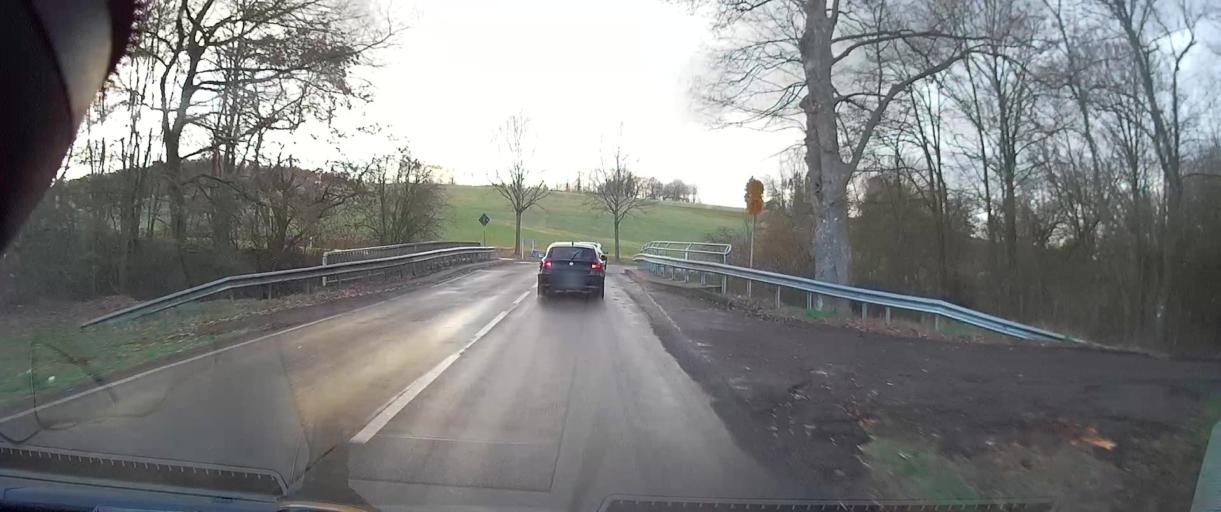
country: DE
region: Rheinland-Pfalz
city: Vielbach
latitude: 50.5229
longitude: 7.7599
